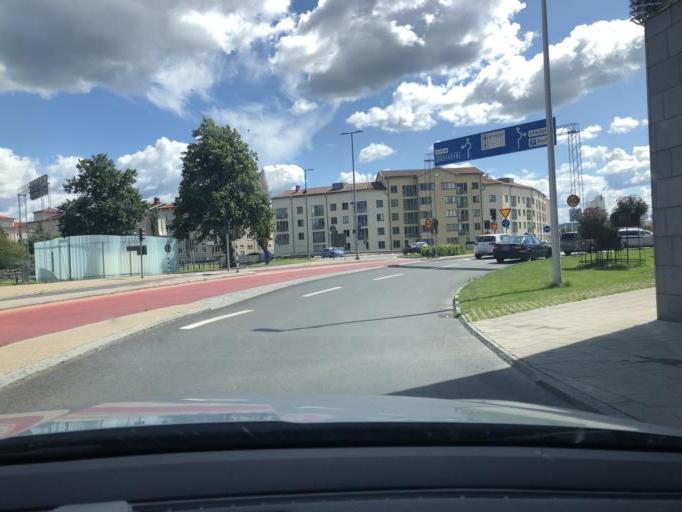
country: SE
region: Joenkoeping
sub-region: Jonkopings Kommun
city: Jonkoping
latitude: 57.7806
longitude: 14.1737
